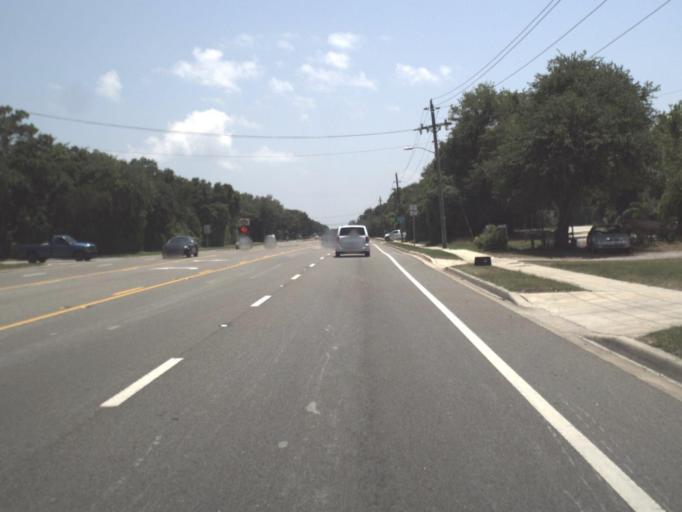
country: US
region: Florida
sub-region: Saint Johns County
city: Saint Augustine
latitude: 29.8773
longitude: -81.2859
